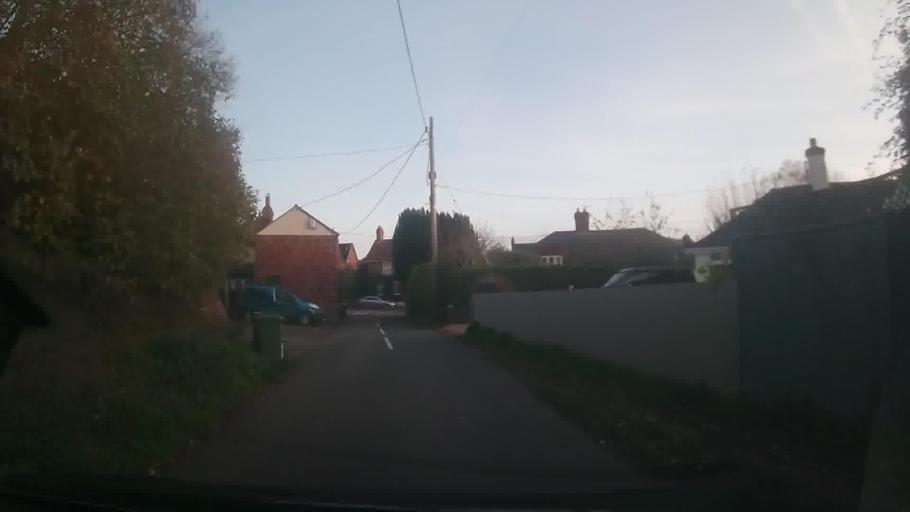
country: GB
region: England
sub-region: Shropshire
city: Petton
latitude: 52.8111
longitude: -2.7886
